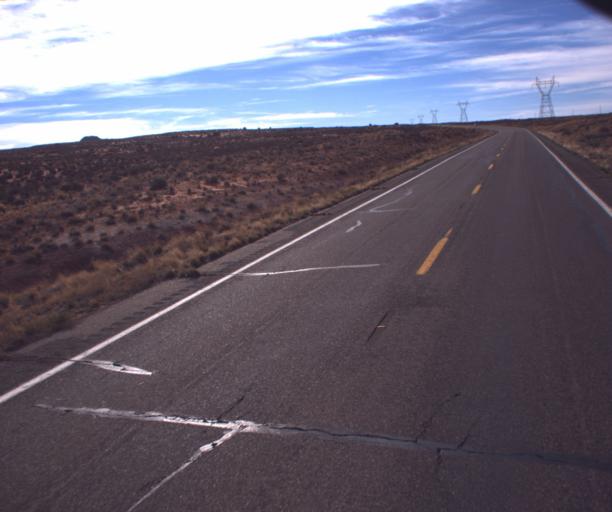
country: US
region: Arizona
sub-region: Coconino County
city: LeChee
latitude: 36.8588
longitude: -111.3377
